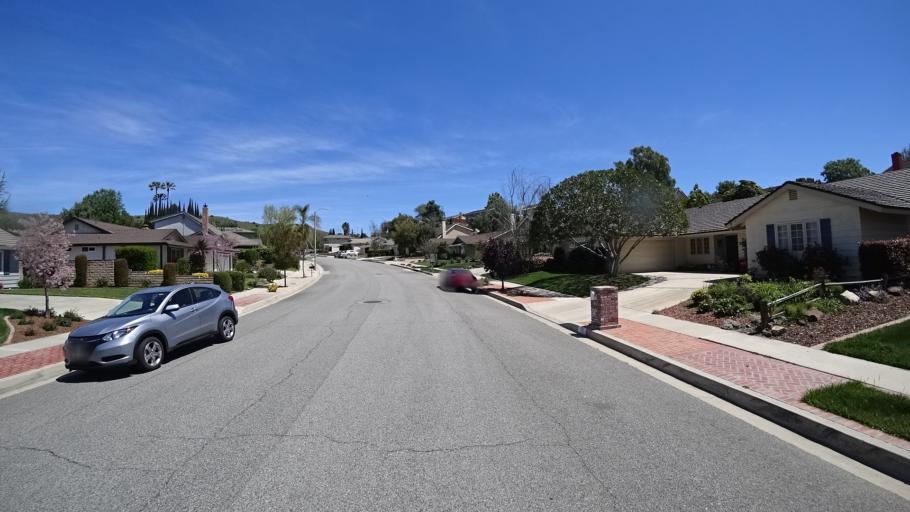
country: US
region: California
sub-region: Ventura County
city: Moorpark
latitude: 34.2305
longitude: -118.8736
